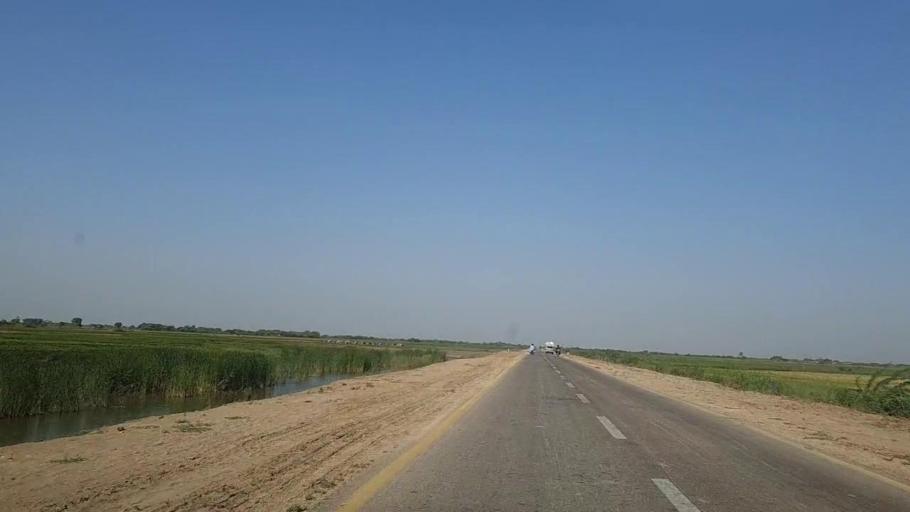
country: PK
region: Sindh
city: Jati
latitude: 24.4185
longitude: 68.3047
